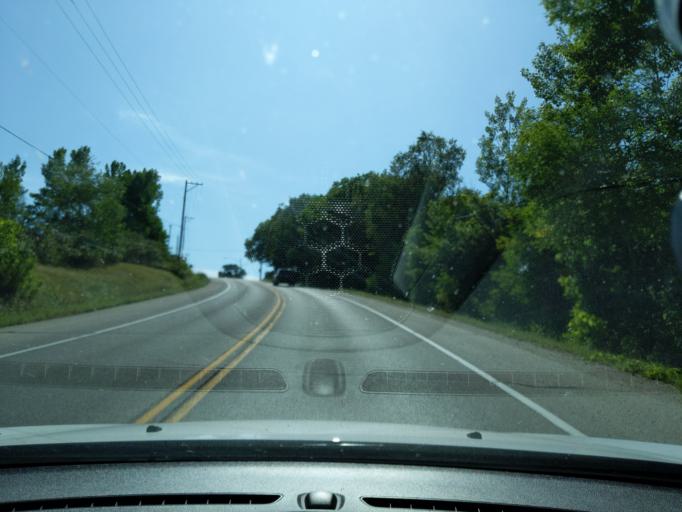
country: US
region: Michigan
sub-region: Delta County
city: Escanaba
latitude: 45.2492
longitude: -87.0821
